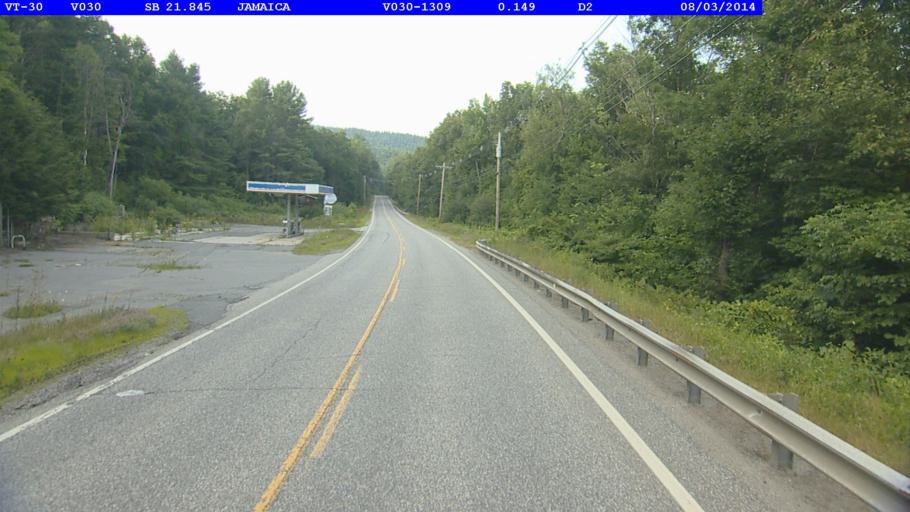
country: US
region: Vermont
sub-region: Windham County
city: Newfane
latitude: 43.0781
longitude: -72.7253
